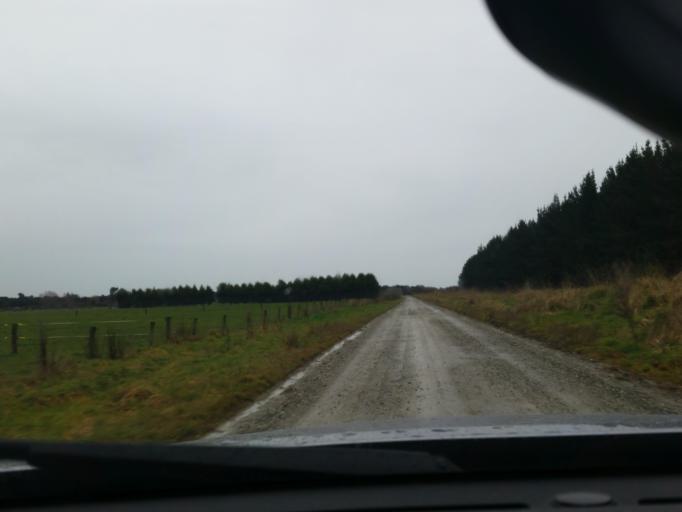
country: NZ
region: Southland
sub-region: Southland District
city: Winton
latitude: -46.2370
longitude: 168.4815
